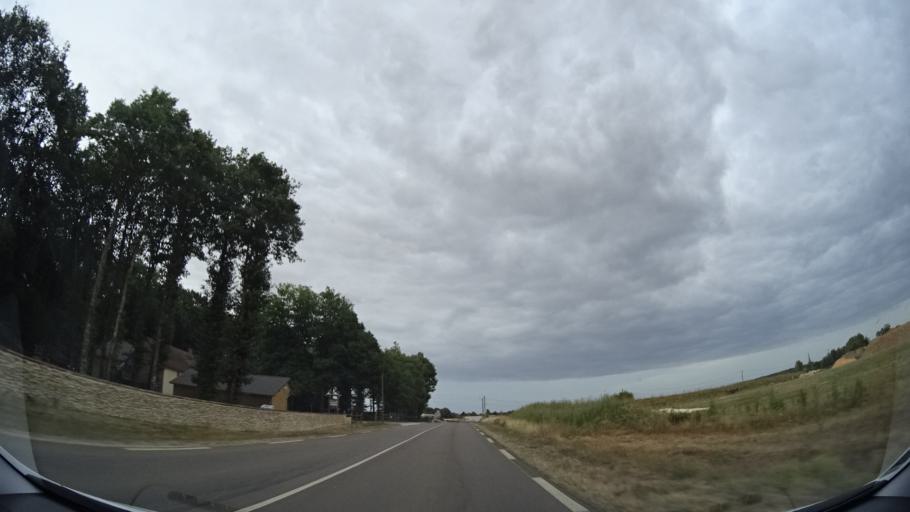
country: FR
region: Bourgogne
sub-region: Departement de l'Yonne
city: Charny
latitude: 47.9414
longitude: 3.1421
